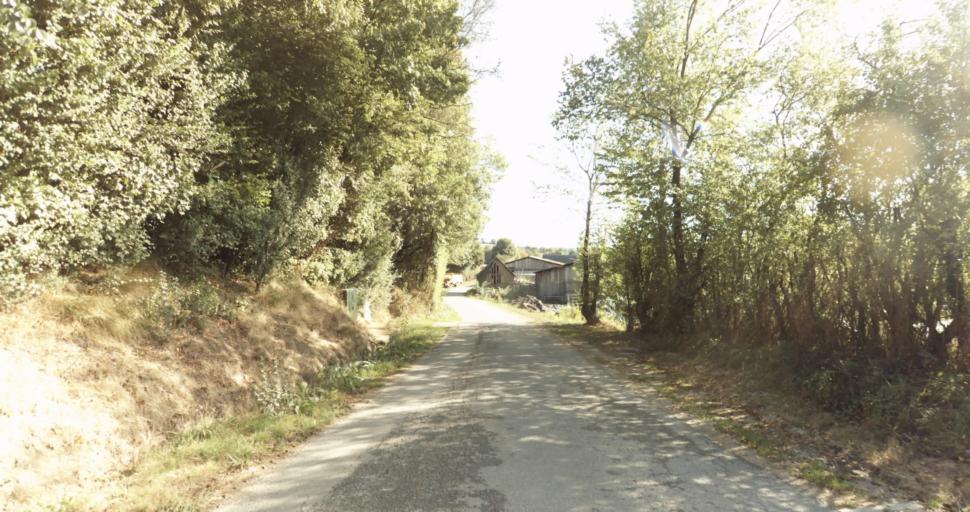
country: FR
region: Lower Normandy
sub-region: Departement de l'Orne
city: Vimoutiers
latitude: 48.9240
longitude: 0.1329
